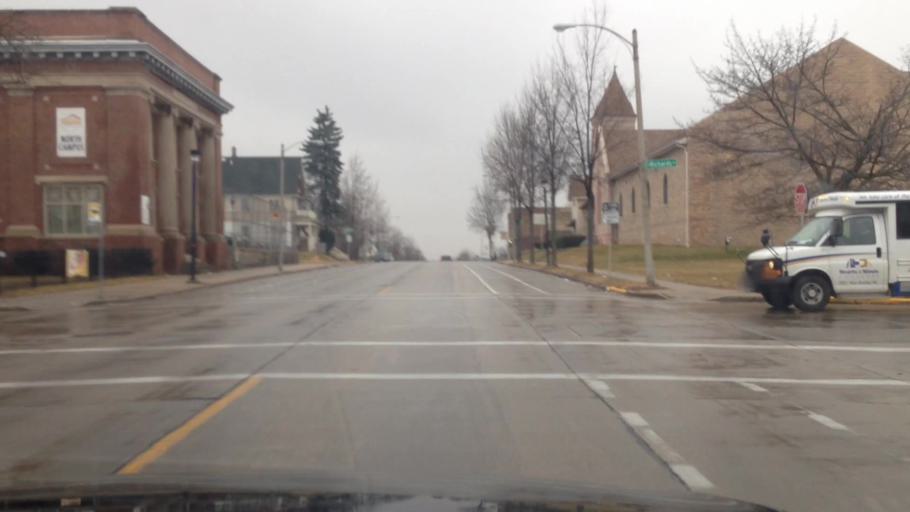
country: US
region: Wisconsin
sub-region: Milwaukee County
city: Milwaukee
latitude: 43.0675
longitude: -87.9076
